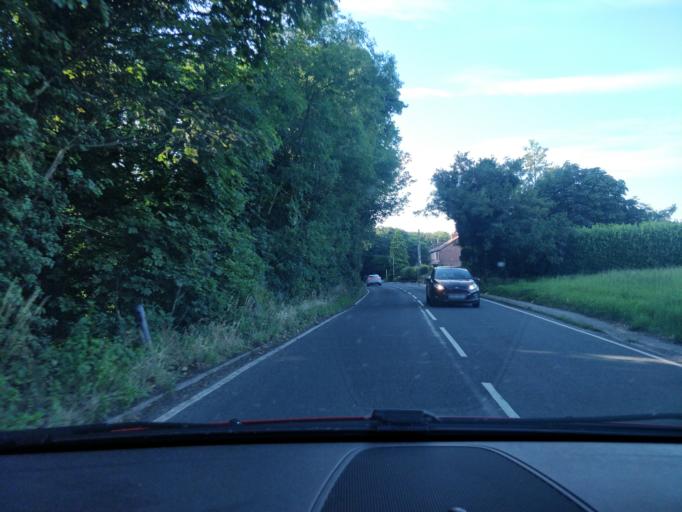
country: GB
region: England
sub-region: Lancashire
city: Banks
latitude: 53.6537
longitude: -2.8780
